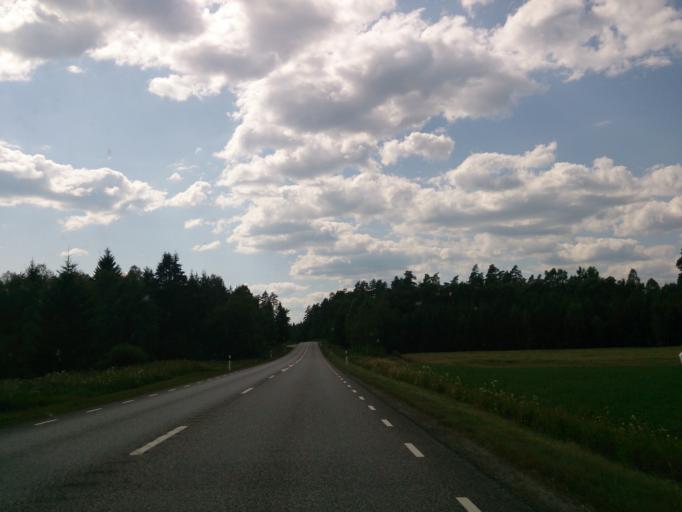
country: SE
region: Joenkoeping
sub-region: Gislaveds Kommun
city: Reftele
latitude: 57.1713
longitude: 13.5847
